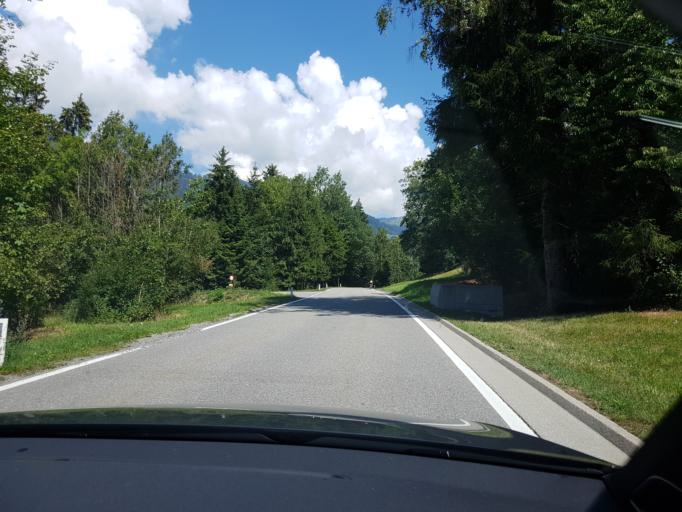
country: AT
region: Vorarlberg
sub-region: Politischer Bezirk Bludenz
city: Ludesch
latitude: 47.2036
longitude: 9.7916
